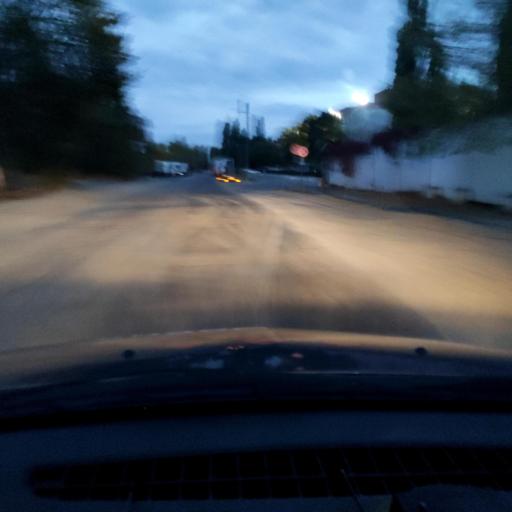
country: RU
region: Voronezj
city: Pridonskoy
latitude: 51.6767
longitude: 39.0922
